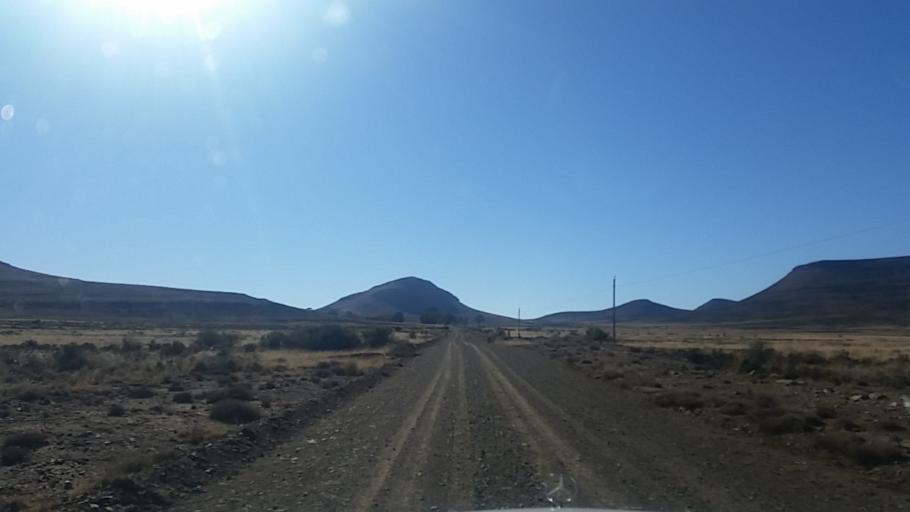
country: ZA
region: Eastern Cape
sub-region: Chris Hani District Municipality
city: Middelburg
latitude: -31.7973
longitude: 24.7175
